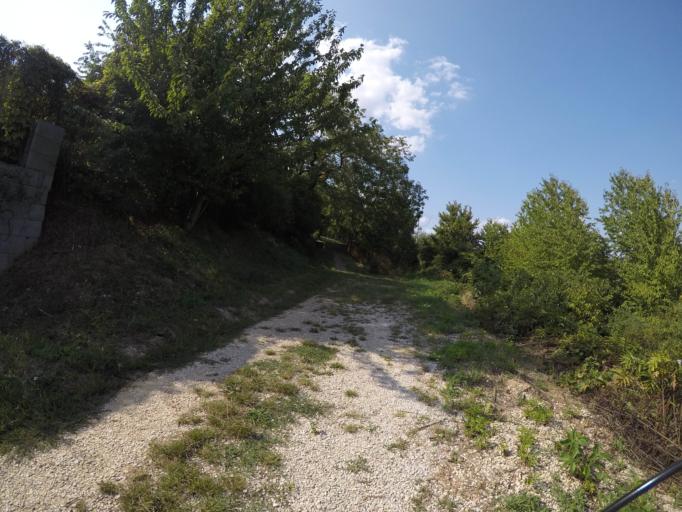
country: SK
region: Trenciansky
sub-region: Okres Nove Mesto nad Vahom
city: Nove Mesto nad Vahom
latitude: 48.7653
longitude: 17.8183
